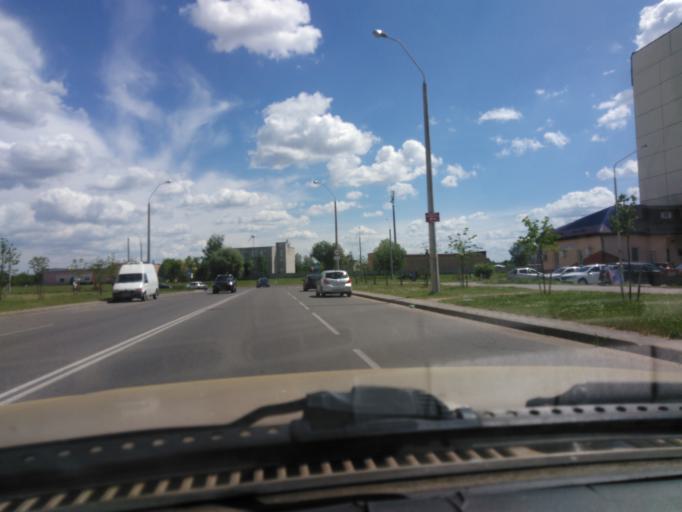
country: BY
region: Mogilev
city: Mahilyow
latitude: 53.9144
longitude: 30.2856
